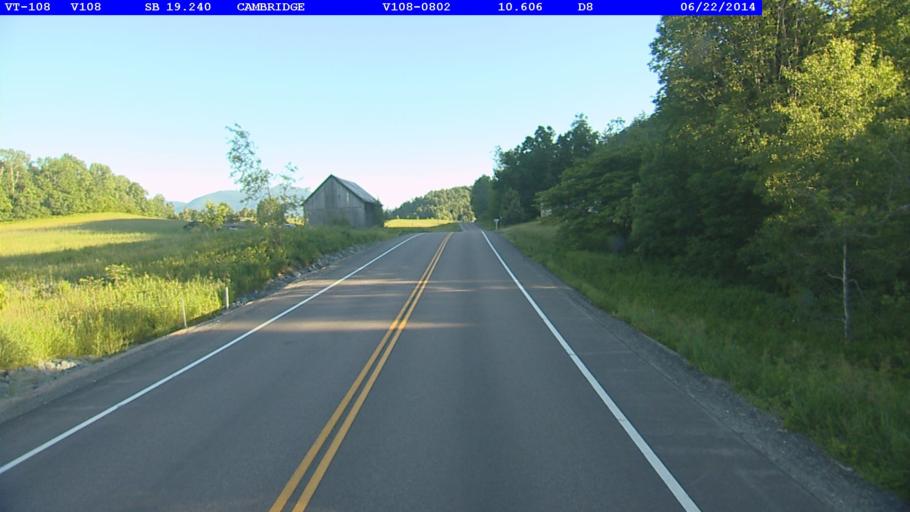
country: US
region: Vermont
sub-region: Lamoille County
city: Johnson
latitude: 44.6684
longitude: -72.8281
